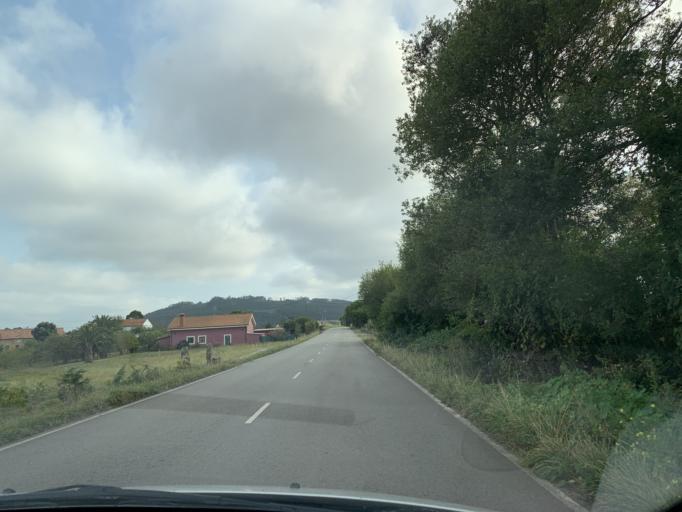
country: ES
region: Asturias
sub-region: Province of Asturias
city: Villaviciosa
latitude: 43.5316
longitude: -5.4293
